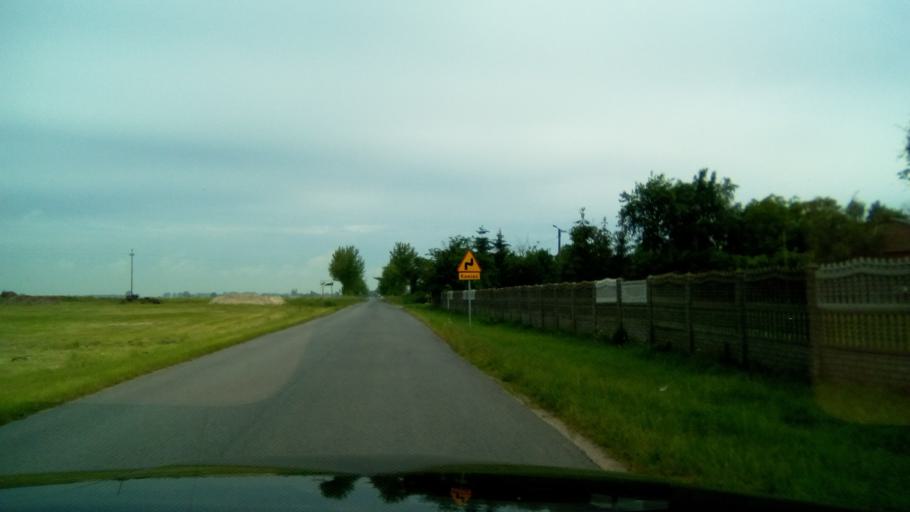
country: PL
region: Greater Poland Voivodeship
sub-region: Powiat gnieznienski
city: Mieleszyn
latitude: 52.6913
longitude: 17.5151
